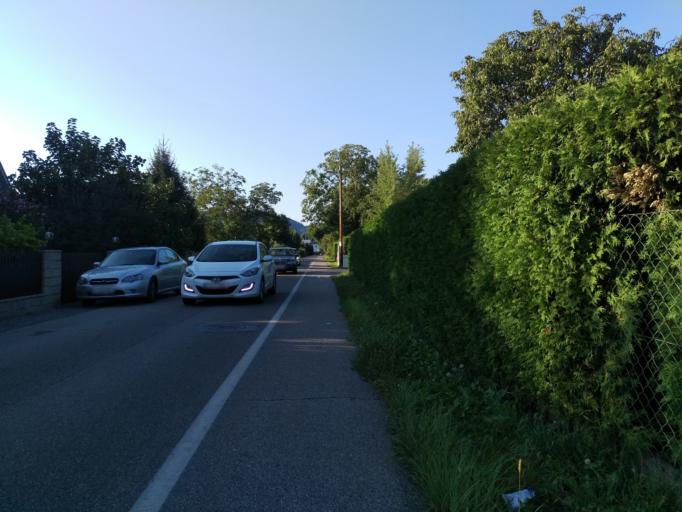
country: AT
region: Styria
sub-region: Graz Stadt
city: Wetzelsdorf
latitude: 47.0408
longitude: 15.4086
